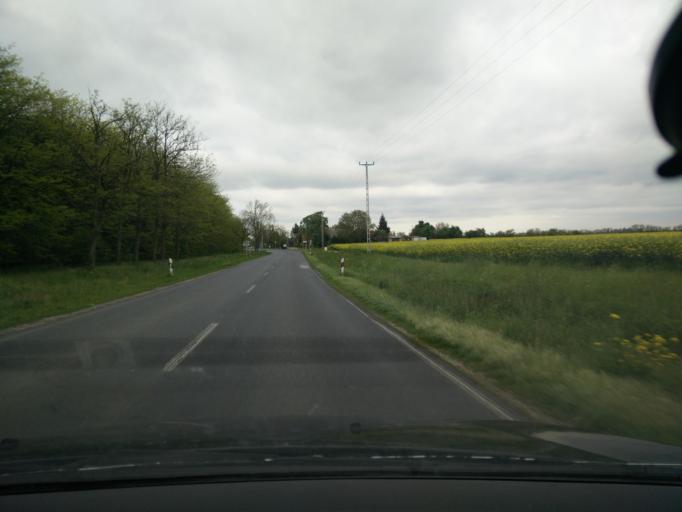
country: HU
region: Veszprem
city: Papa
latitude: 47.3873
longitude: 17.4724
